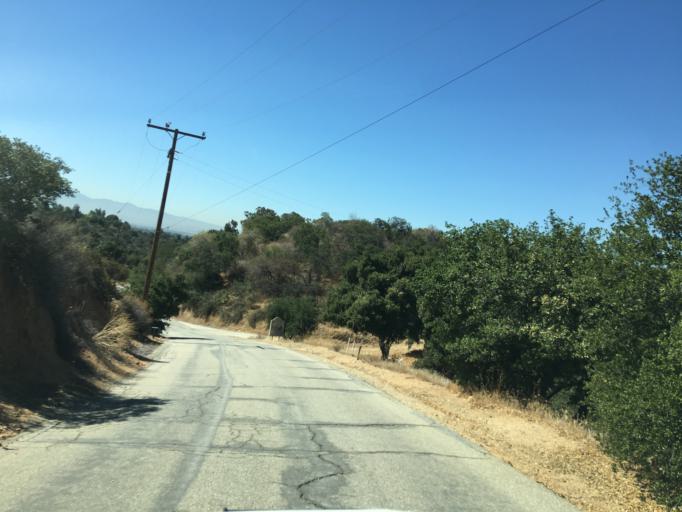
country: US
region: California
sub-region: Los Angeles County
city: La Verne
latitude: 34.1325
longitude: -117.7436
